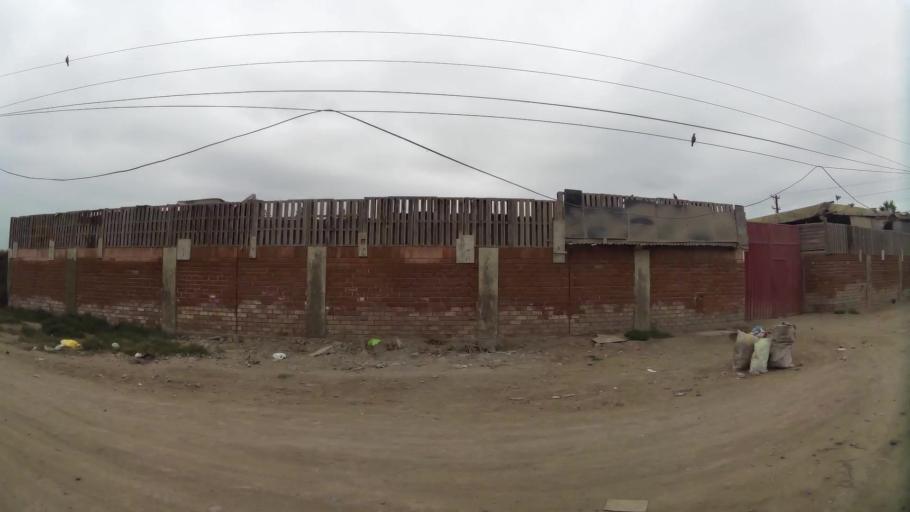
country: PE
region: Lima
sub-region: Lima
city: Surco
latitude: -12.2067
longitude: -77.0043
